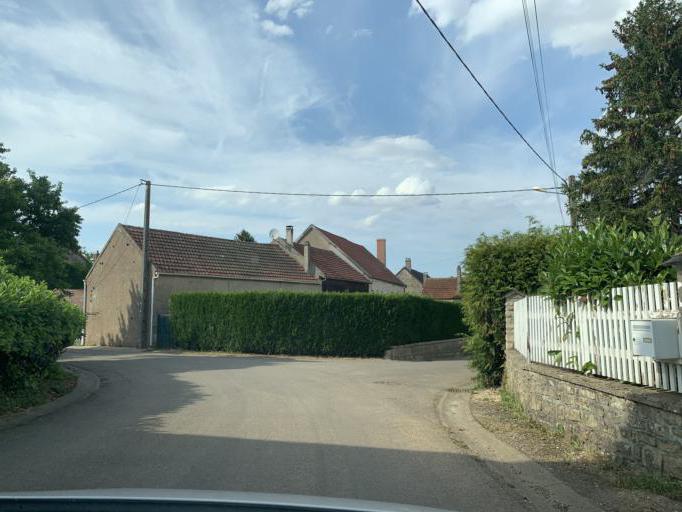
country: FR
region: Bourgogne
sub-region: Departement de l'Yonne
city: Fontenailles
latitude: 47.5175
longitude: 3.4279
